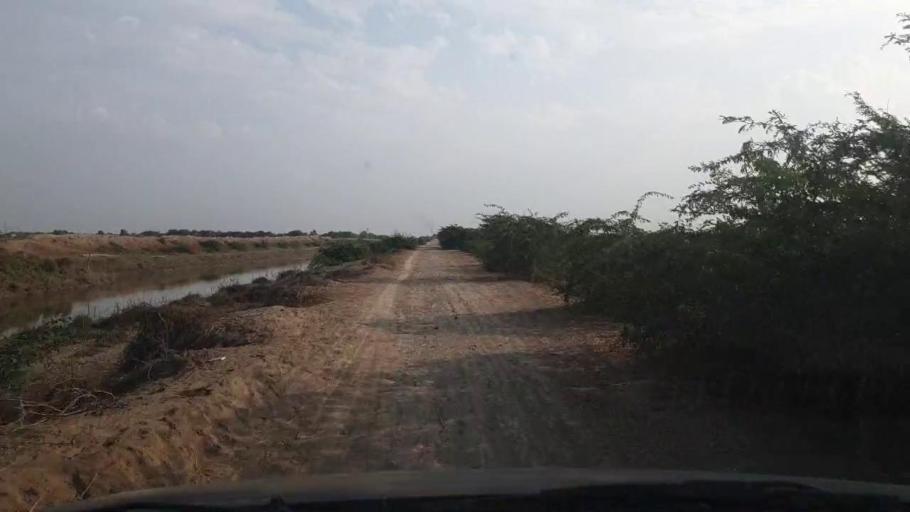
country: PK
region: Sindh
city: Badin
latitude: 24.5542
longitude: 68.6700
